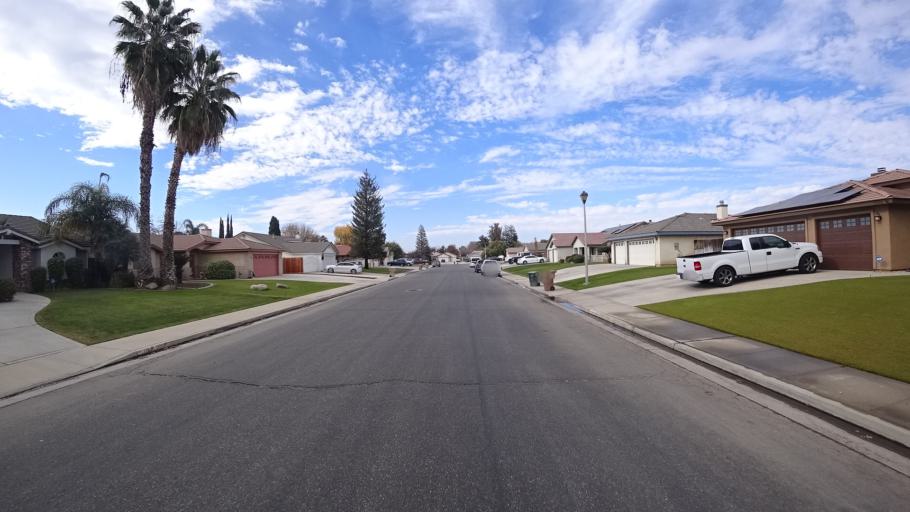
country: US
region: California
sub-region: Kern County
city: Rosedale
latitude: 35.3970
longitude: -119.1343
